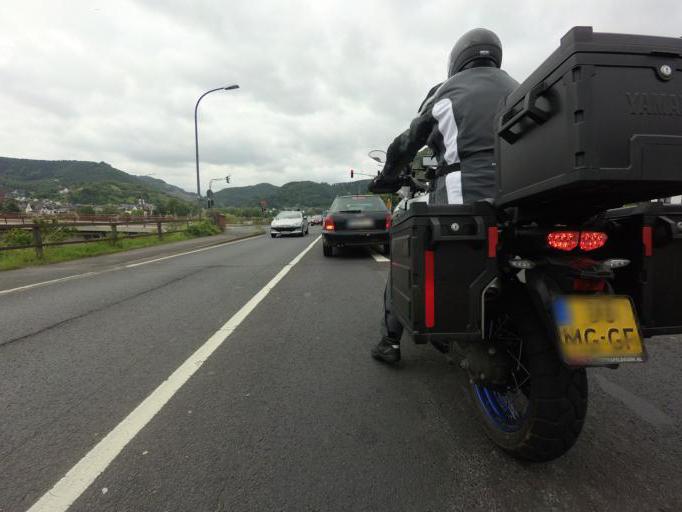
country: DE
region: Rheinland-Pfalz
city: Treis-Karden
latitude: 50.1784
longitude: 7.2986
